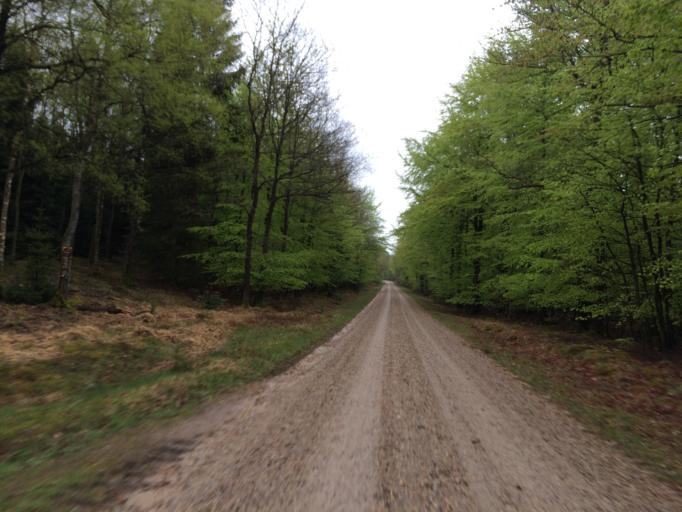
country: DK
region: Central Jutland
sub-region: Holstebro Kommune
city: Ulfborg
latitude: 56.2555
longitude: 8.4562
